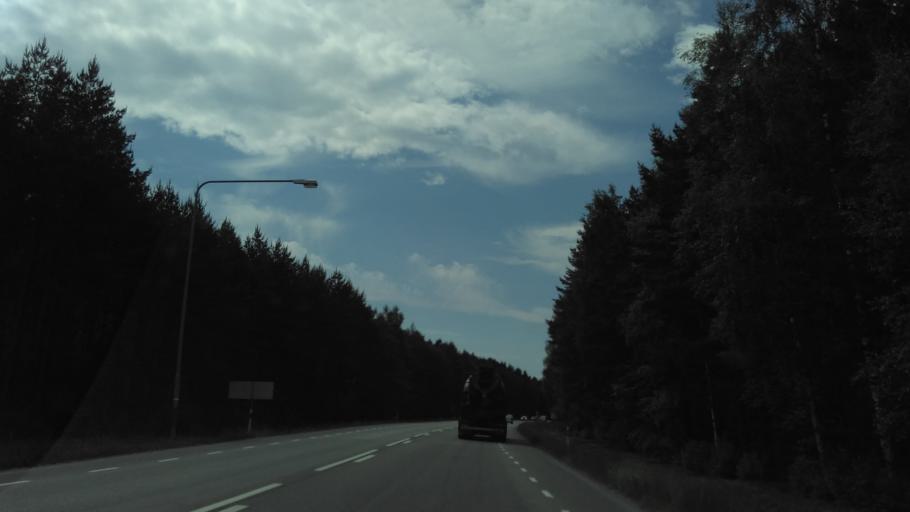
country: SE
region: Vaestra Goetaland
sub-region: Lidkopings Kommun
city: Lidkoping
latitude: 58.4885
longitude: 13.1847
